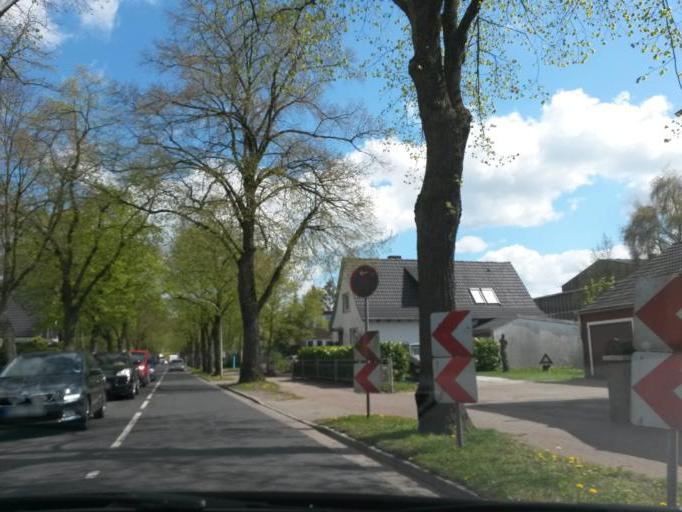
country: DE
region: Schleswig-Holstein
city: Uetersen
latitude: 53.6833
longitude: 9.6784
